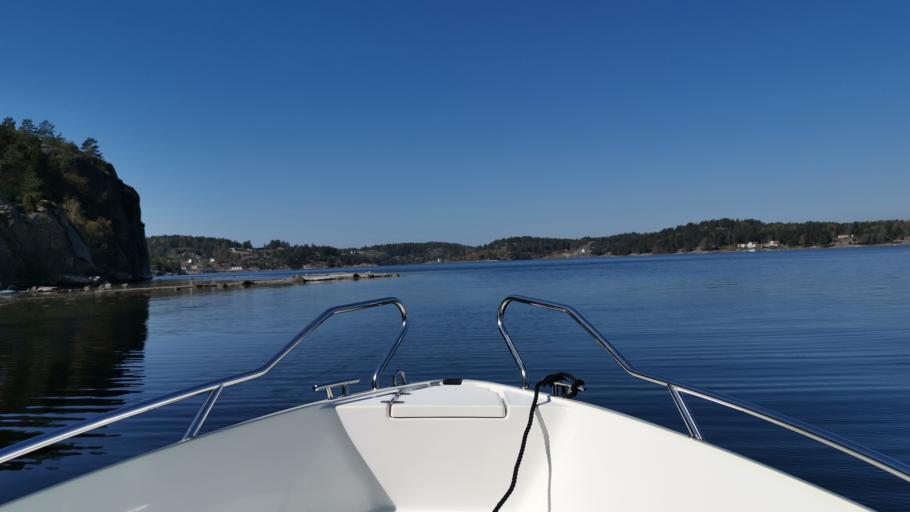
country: SE
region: Vaestra Goetaland
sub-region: Orust
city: Henan
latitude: 58.2560
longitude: 11.5793
